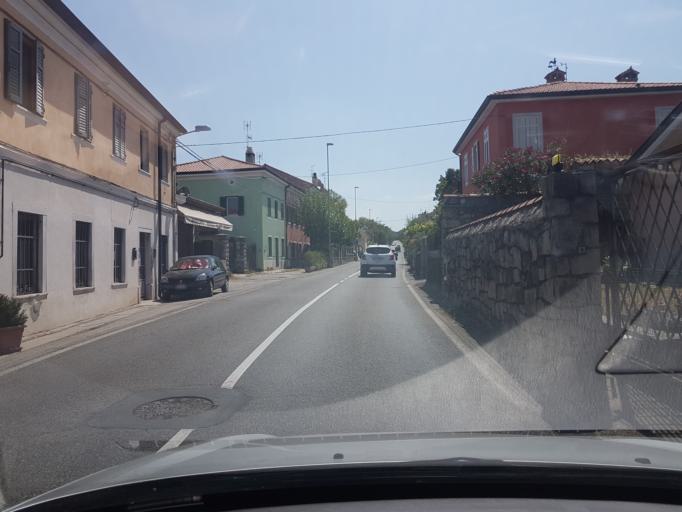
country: IT
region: Friuli Venezia Giulia
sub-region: Provincia di Trieste
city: Aurisina
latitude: 45.7496
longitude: 13.6725
